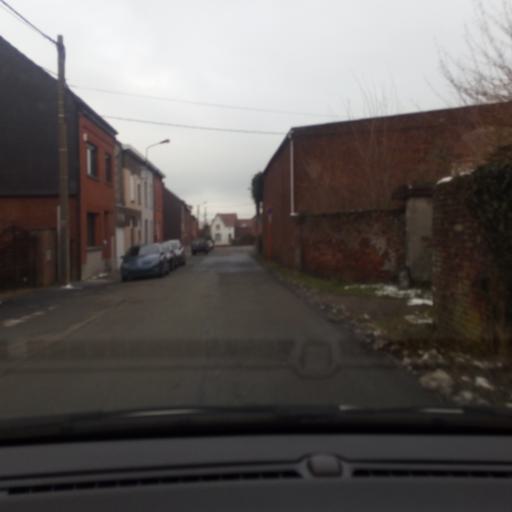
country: BE
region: Wallonia
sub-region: Province du Hainaut
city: Dour
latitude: 50.3933
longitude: 3.7803
